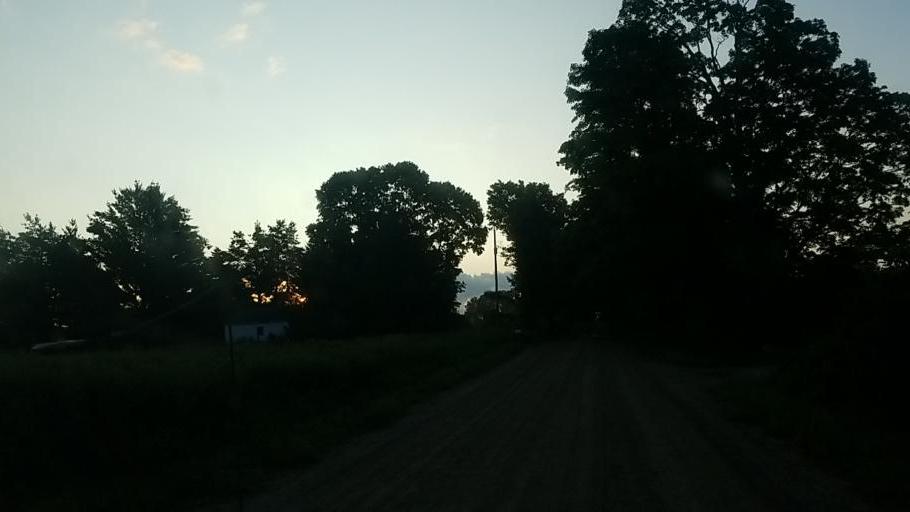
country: US
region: Michigan
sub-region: Osceola County
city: Evart
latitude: 43.9151
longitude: -85.1917
